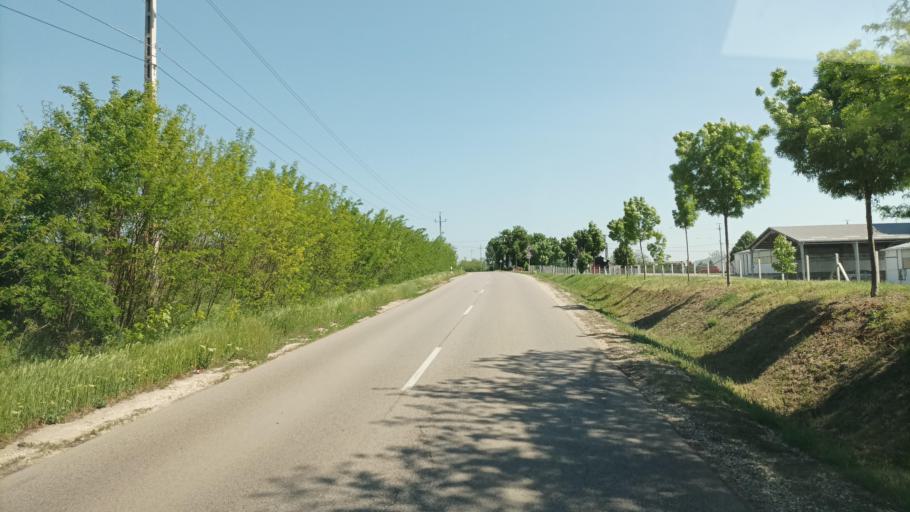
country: HU
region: Pest
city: Suelysap
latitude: 47.4338
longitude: 19.5327
